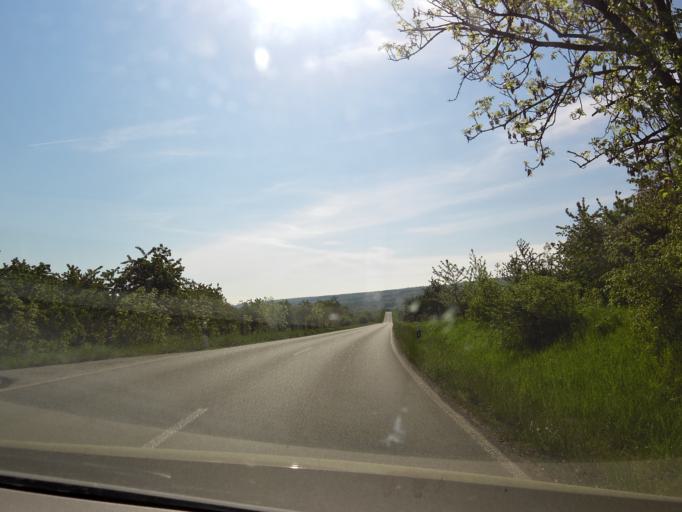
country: DE
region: Thuringia
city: Gierstadt
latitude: 51.0437
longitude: 10.8318
